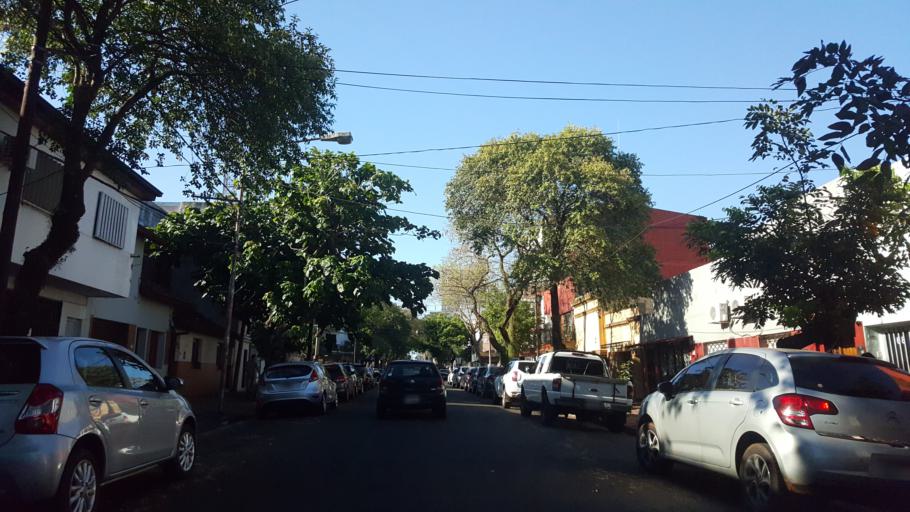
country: AR
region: Misiones
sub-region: Departamento de Capital
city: Posadas
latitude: -27.3624
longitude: -55.8951
